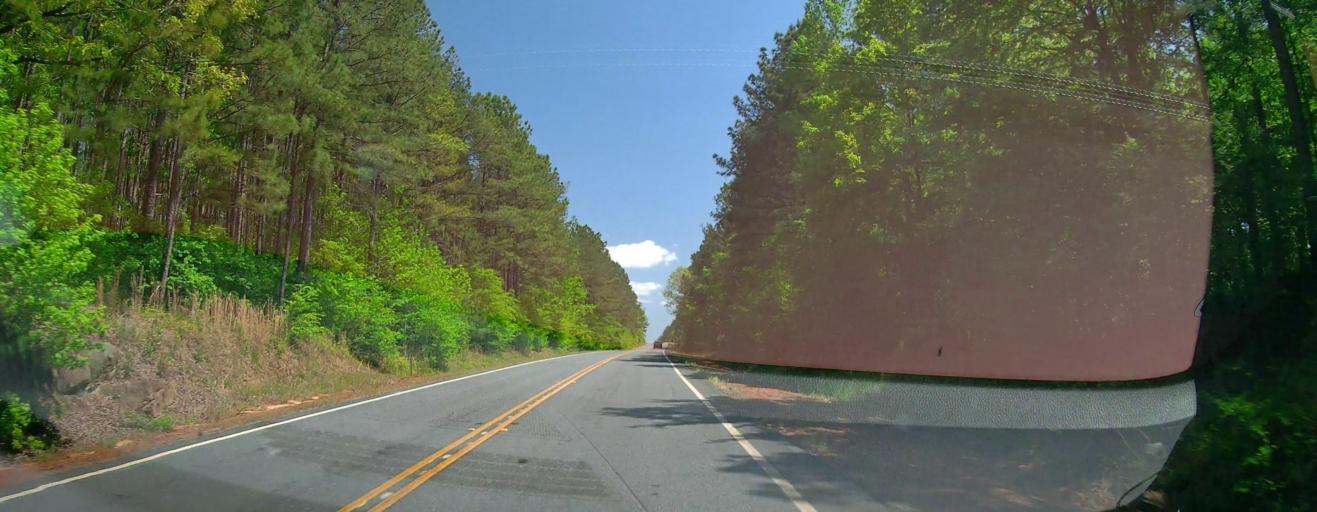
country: US
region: Georgia
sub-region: Putnam County
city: Eatonton
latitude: 33.2174
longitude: -83.4879
